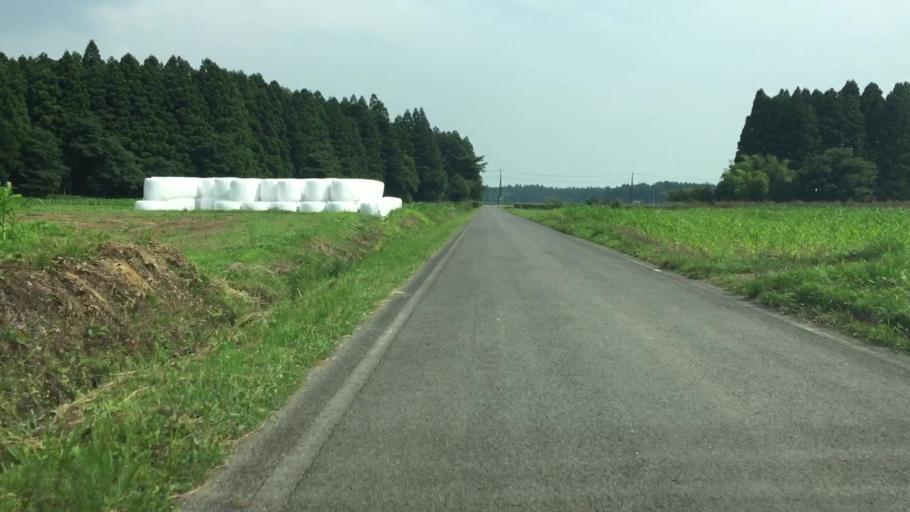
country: JP
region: Tochigi
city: Kuroiso
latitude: 37.0132
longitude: 139.9504
